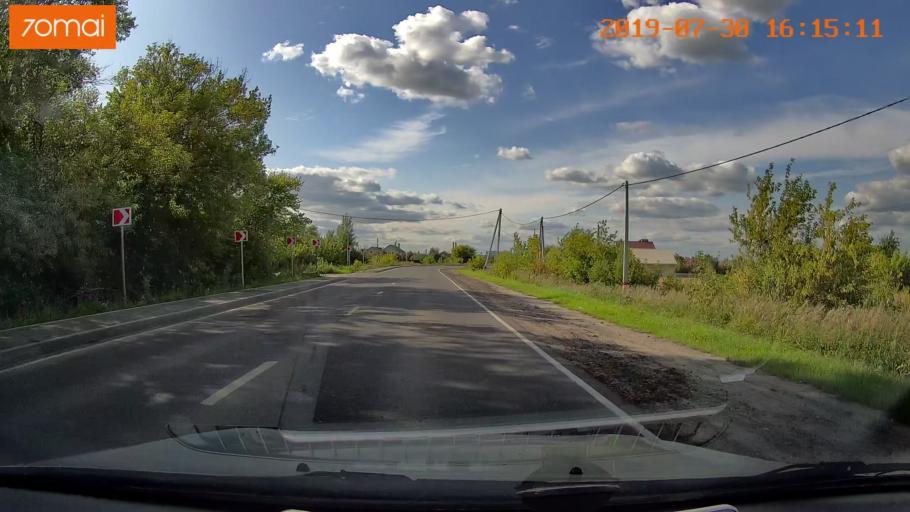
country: RU
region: Moskovskaya
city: Voskresensk
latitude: 55.2942
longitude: 38.6701
